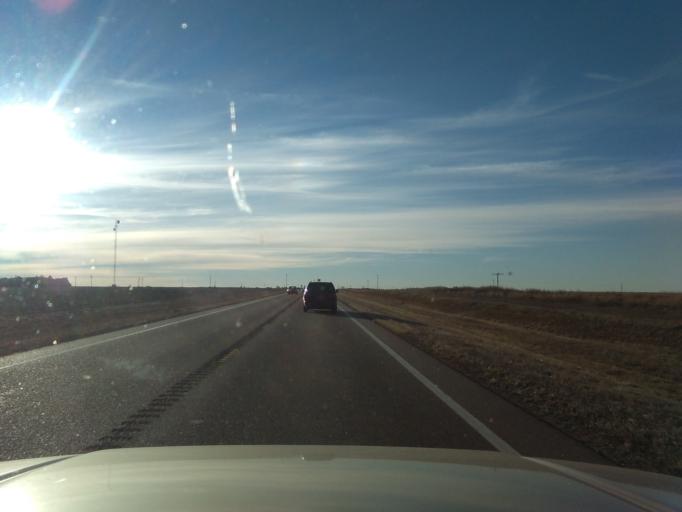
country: US
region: Kansas
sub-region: Thomas County
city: Colby
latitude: 39.4561
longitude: -100.7894
